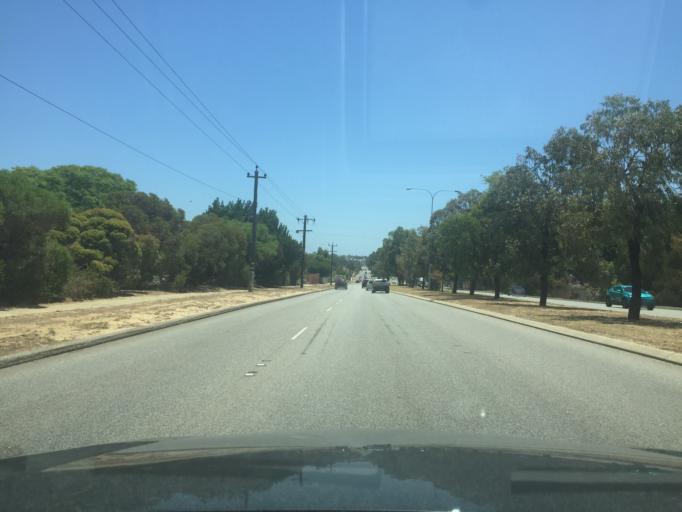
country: AU
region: Western Australia
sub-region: Fremantle
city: Samson
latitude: -32.0665
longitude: 115.8053
